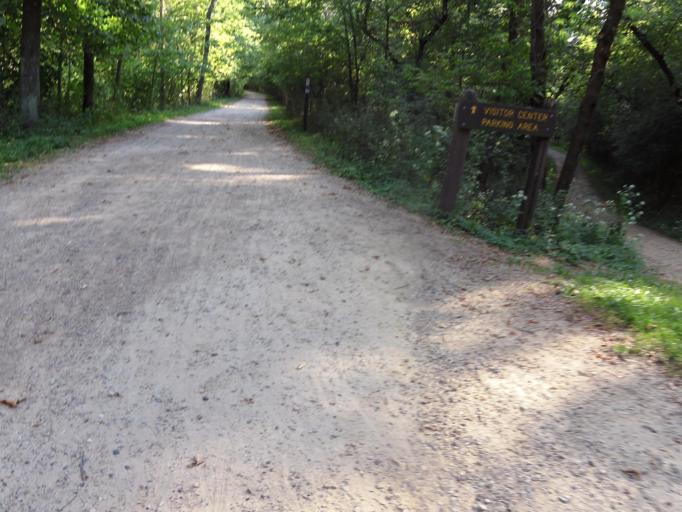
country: US
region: Minnesota
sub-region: Washington County
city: Afton
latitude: 44.8612
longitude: -92.7746
